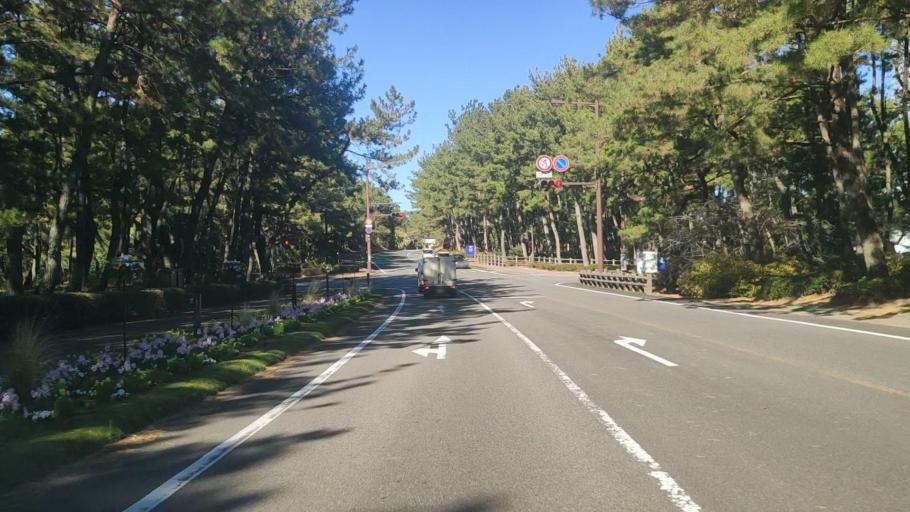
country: JP
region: Miyazaki
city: Miyazaki-shi
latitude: 31.9548
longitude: 131.4673
